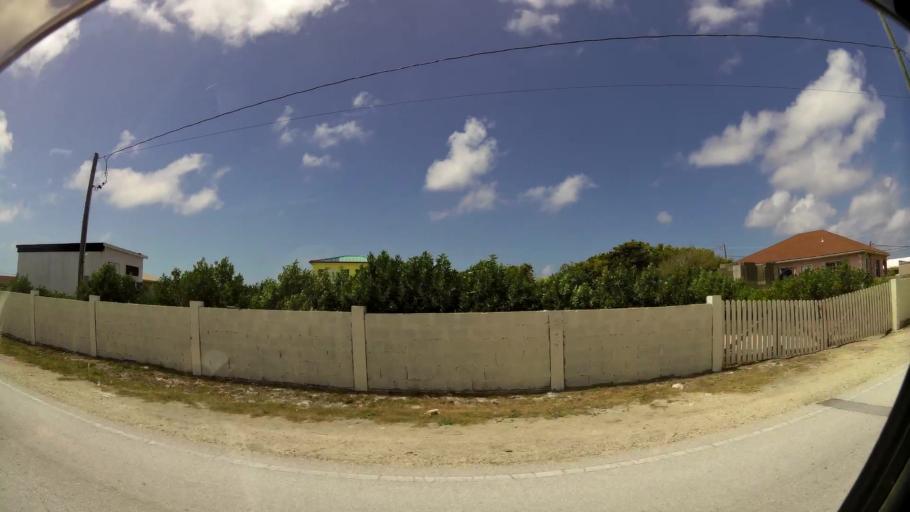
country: TC
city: Cockburn Town
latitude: 21.4594
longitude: -71.1387
